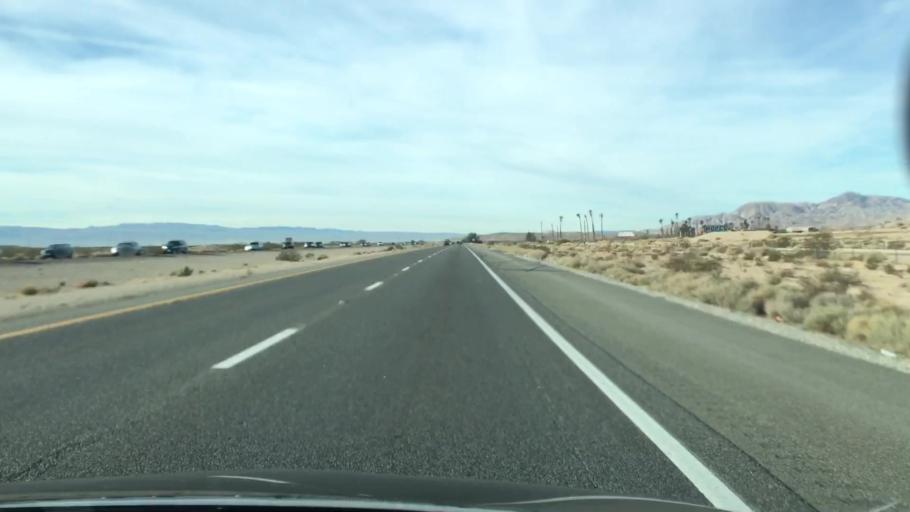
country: US
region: California
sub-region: San Bernardino County
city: Fort Irwin
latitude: 34.9497
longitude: -116.6772
